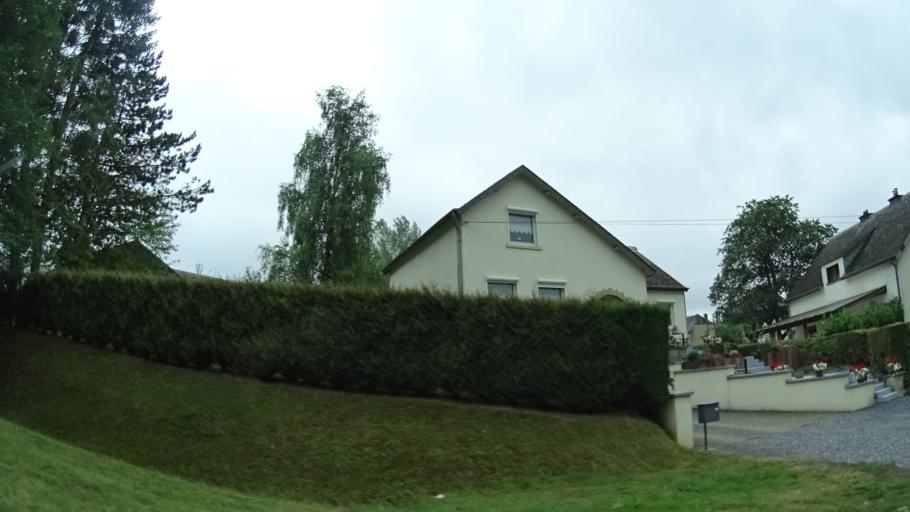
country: BE
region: Wallonia
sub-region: Province du Luxembourg
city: Arlon
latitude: 49.6927
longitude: 5.7697
